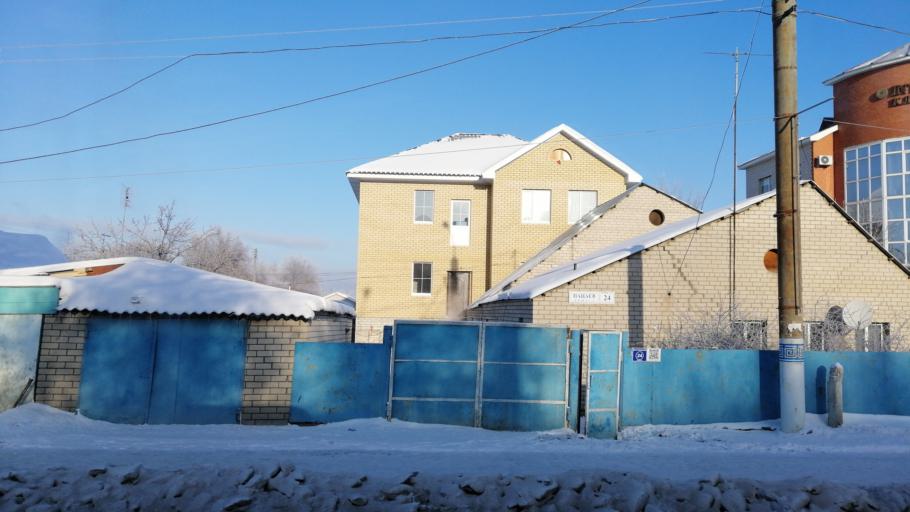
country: KZ
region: Aqtoebe
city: Aqtobe
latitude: 50.2995
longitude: 57.1477
